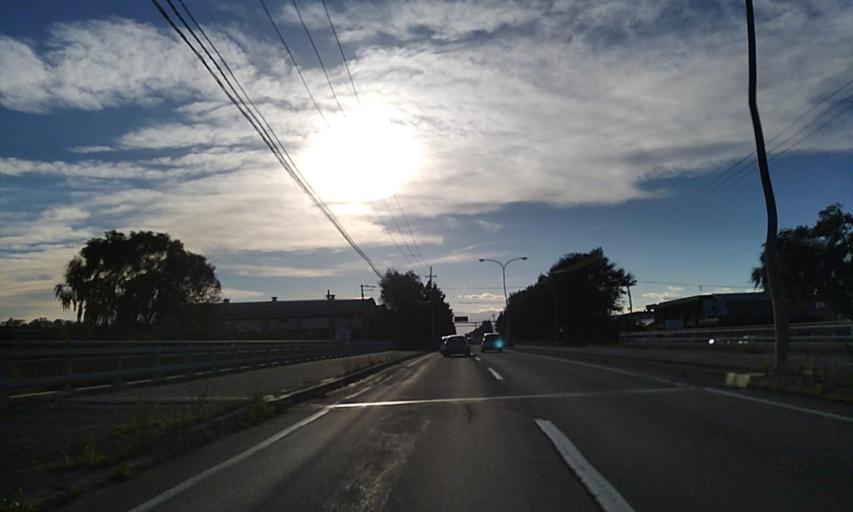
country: JP
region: Hokkaido
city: Obihiro
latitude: 42.9276
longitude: 143.1413
